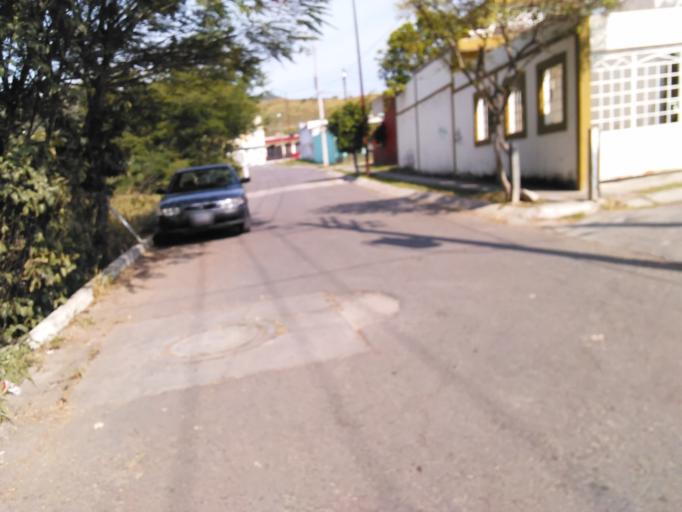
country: MX
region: Nayarit
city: Tepic
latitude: 21.4906
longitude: -104.8537
